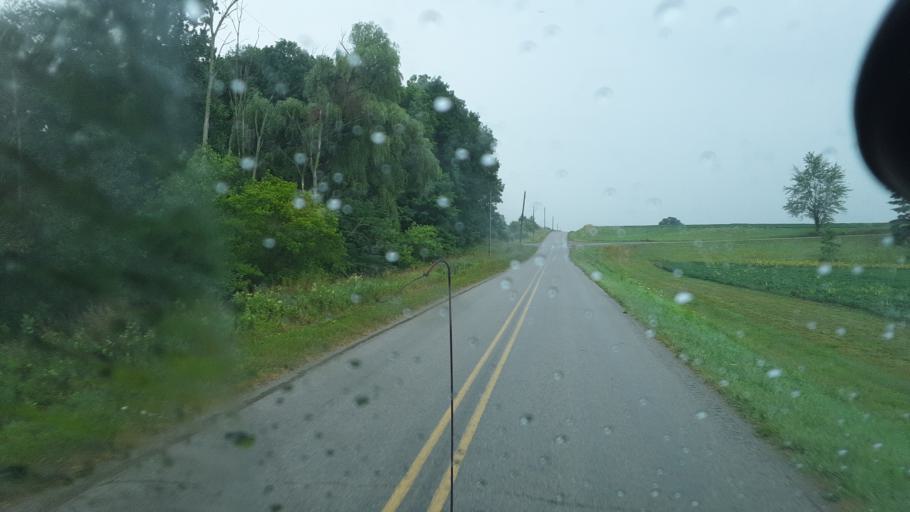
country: US
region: Indiana
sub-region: DeKalb County
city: Butler
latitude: 41.4643
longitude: -84.8141
